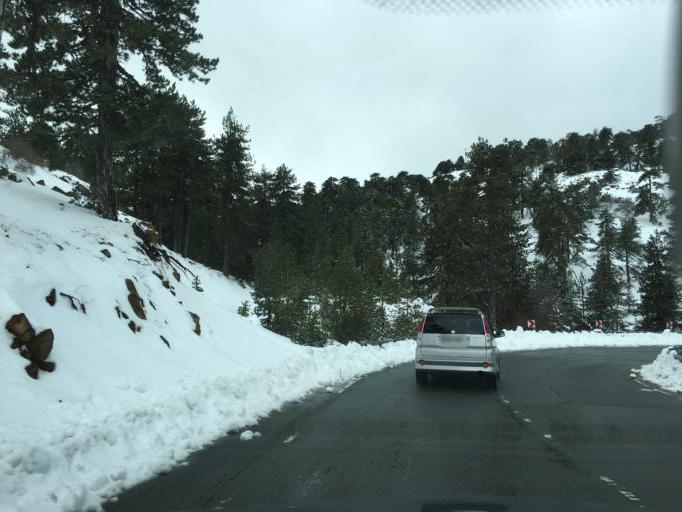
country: CY
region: Lefkosia
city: Kakopetria
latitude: 34.9357
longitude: 32.8717
